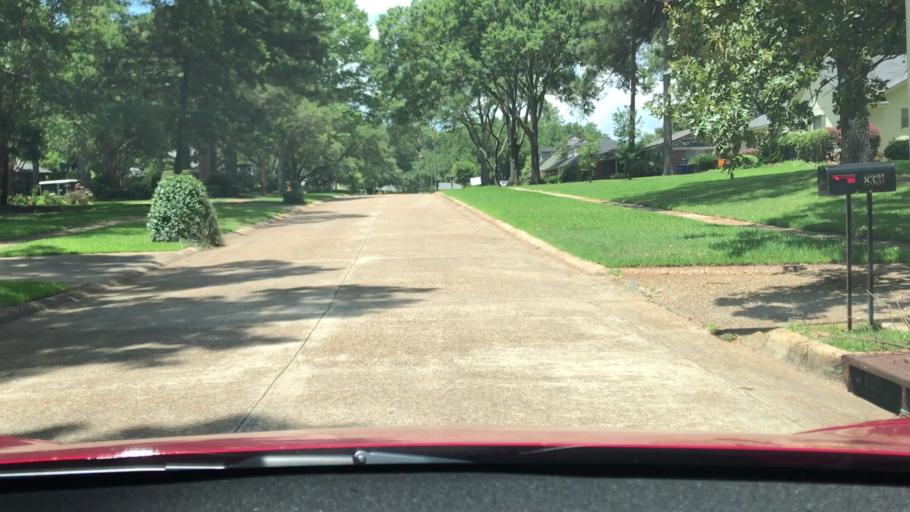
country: US
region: Louisiana
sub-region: Bossier Parish
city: Bossier City
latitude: 32.4309
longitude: -93.7343
